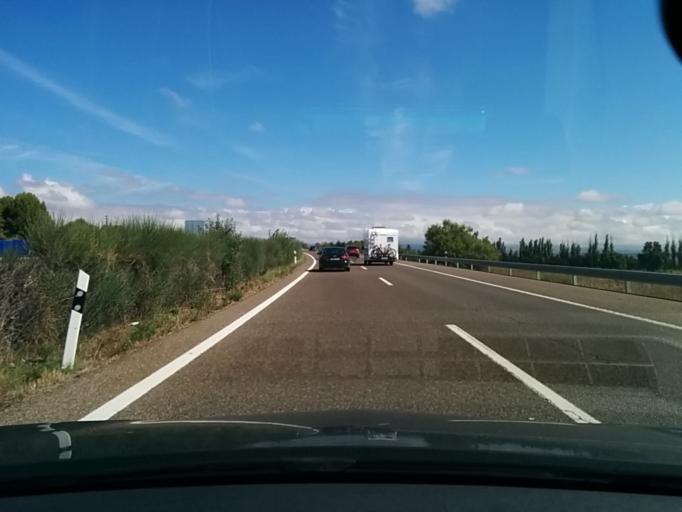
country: ES
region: Aragon
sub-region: Provincia de Huesca
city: Huesca
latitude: 42.1337
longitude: -0.4296
